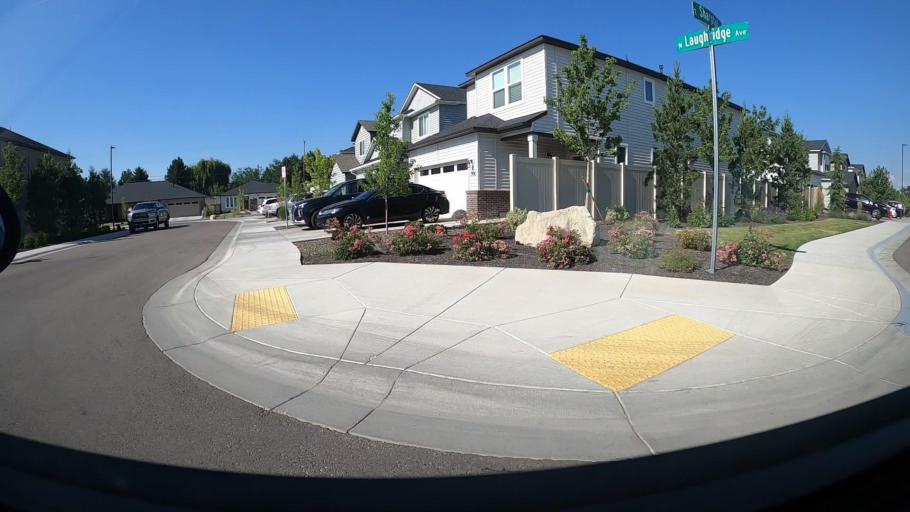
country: US
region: Idaho
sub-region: Ada County
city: Meridian
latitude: 43.6328
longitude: -116.3698
